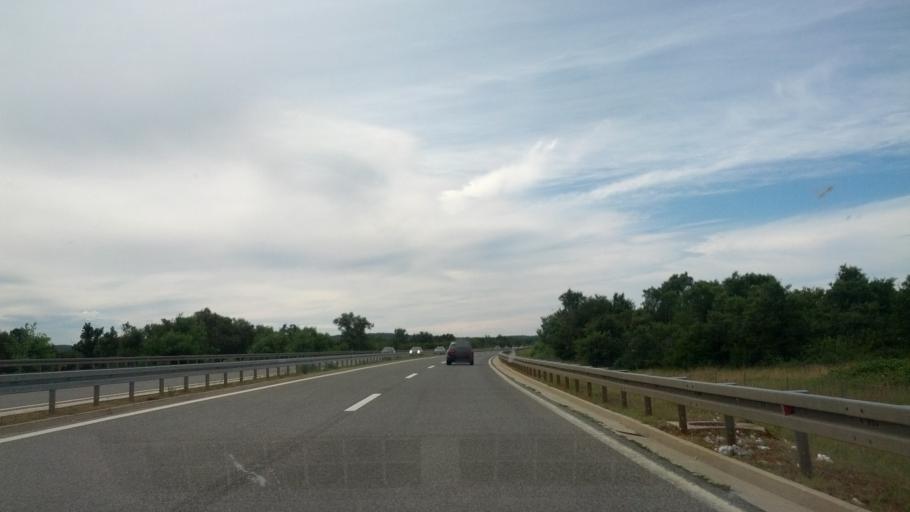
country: HR
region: Istarska
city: Vrsar
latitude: 45.1745
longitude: 13.7337
